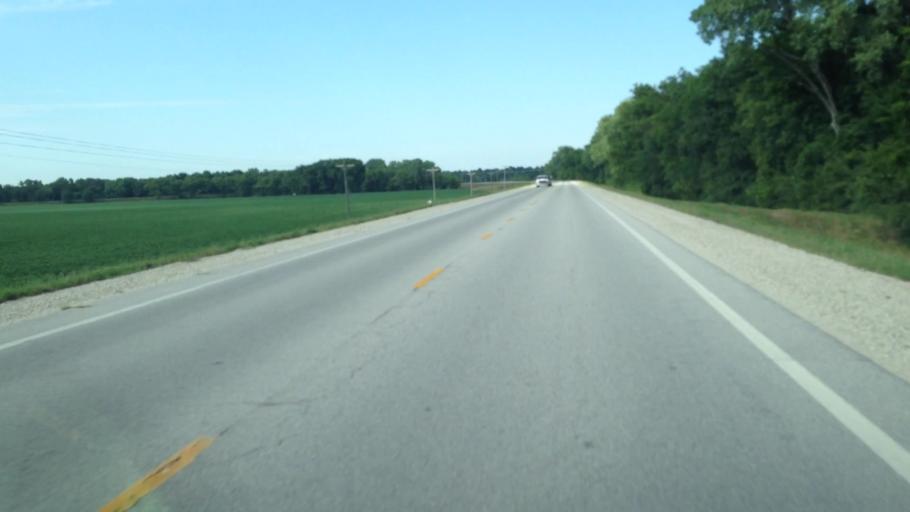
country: US
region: Kansas
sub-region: Neosho County
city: Erie
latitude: 37.5559
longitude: -95.2584
